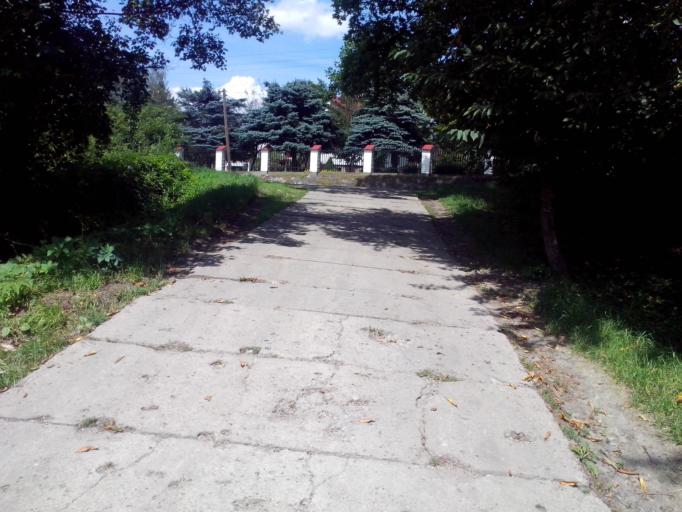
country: PL
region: Subcarpathian Voivodeship
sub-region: Powiat strzyzowski
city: Strzyzow
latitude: 49.8699
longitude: 21.8062
